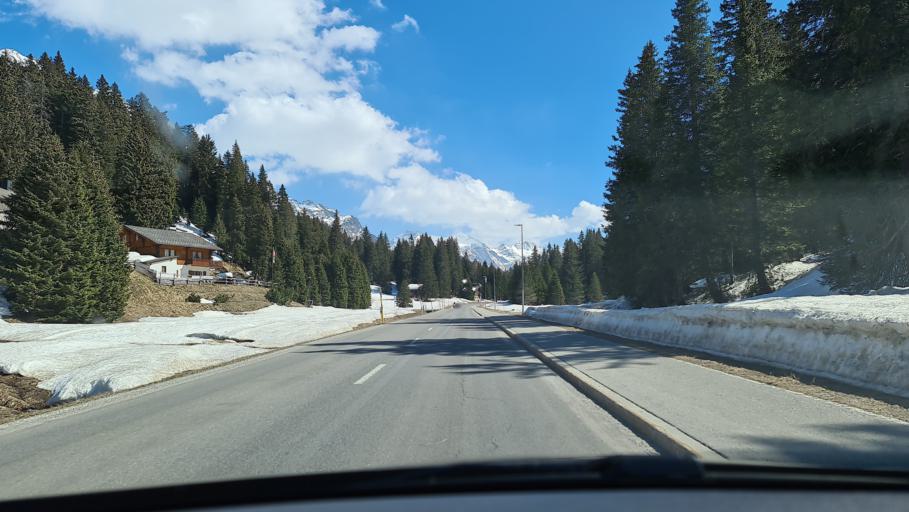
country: CH
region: Grisons
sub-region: Hinterrhein District
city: Hinterrhein
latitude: 46.4573
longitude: 9.1958
